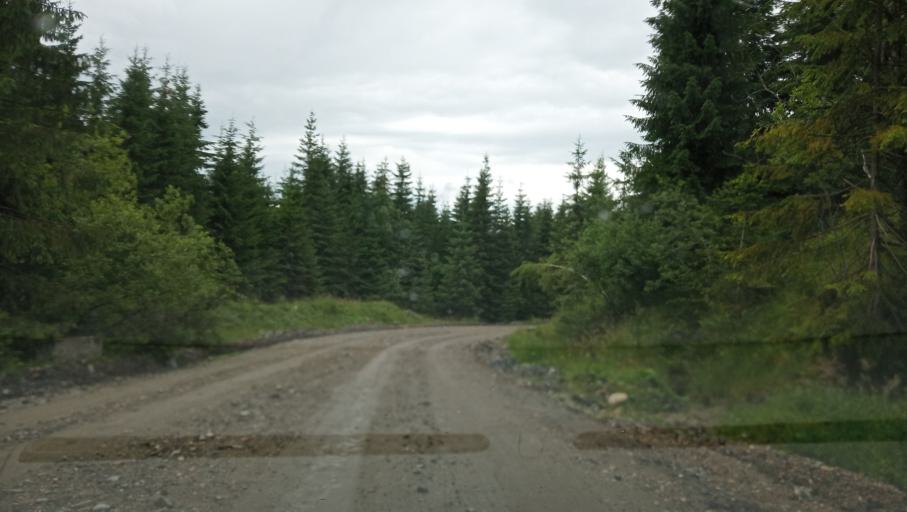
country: RO
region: Hunedoara
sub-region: Oras Petrila
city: Petrila
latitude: 45.4013
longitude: 23.5692
